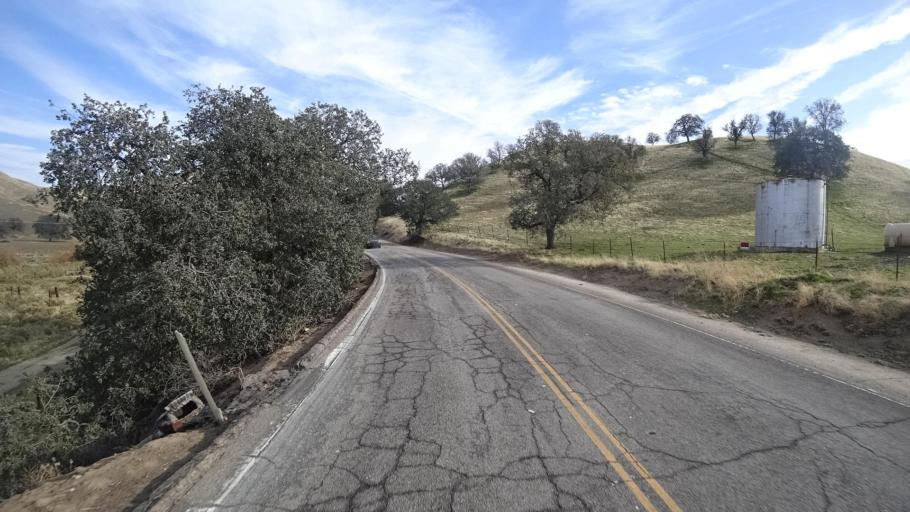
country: US
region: California
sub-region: Kern County
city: Bear Valley Springs
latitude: 35.2853
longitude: -118.6253
